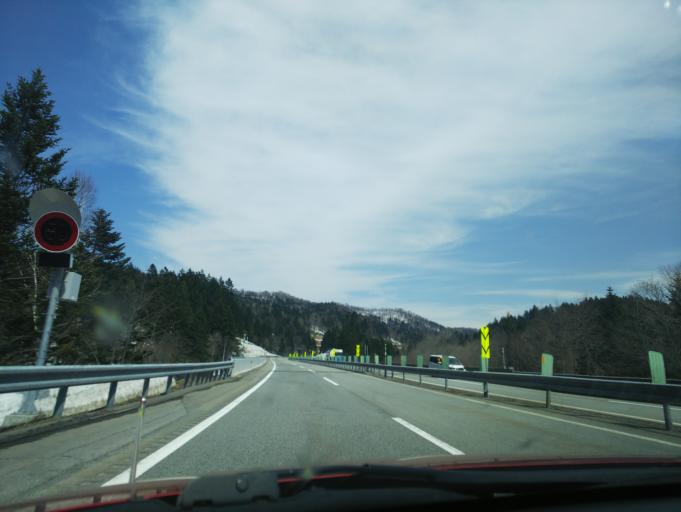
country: JP
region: Hokkaido
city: Fukagawa
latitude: 43.7770
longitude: 142.1933
